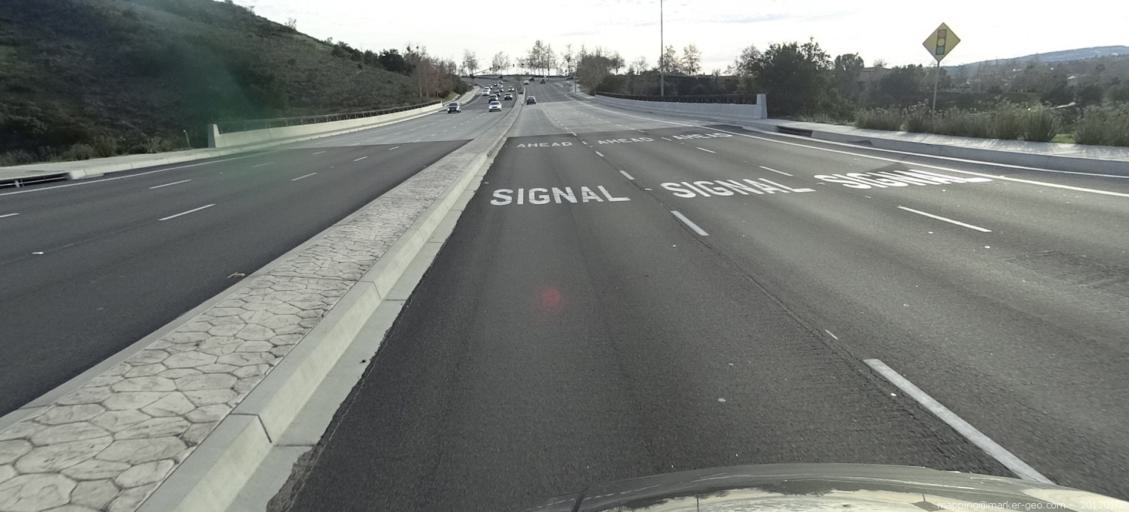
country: US
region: California
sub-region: Orange County
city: Ladera Ranch
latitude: 33.5775
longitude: -117.6325
